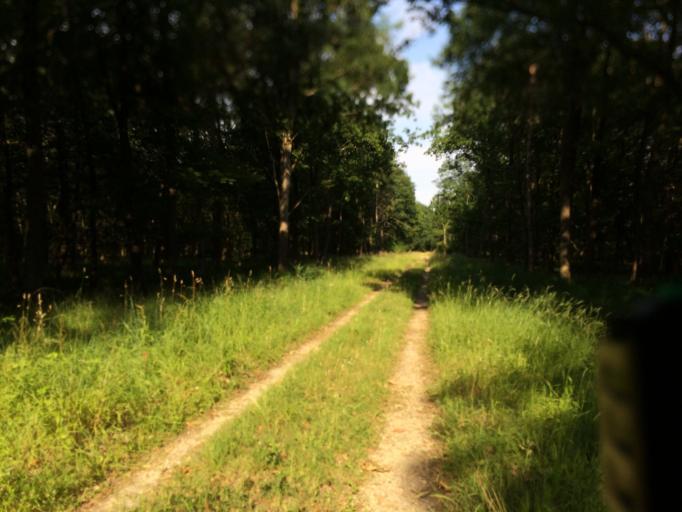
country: FR
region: Ile-de-France
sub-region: Departement de l'Essonne
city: Tigery
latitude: 48.6664
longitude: 2.4993
